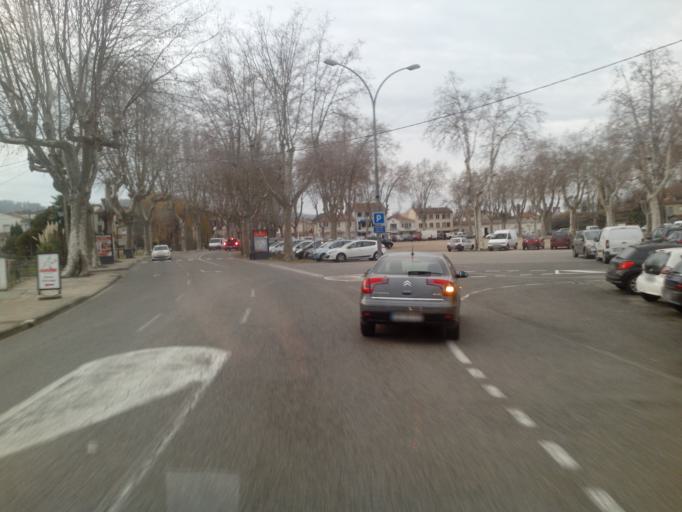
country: FR
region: Midi-Pyrenees
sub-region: Departement de l'Ariege
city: Pamiers
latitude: 43.1183
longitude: 1.6142
